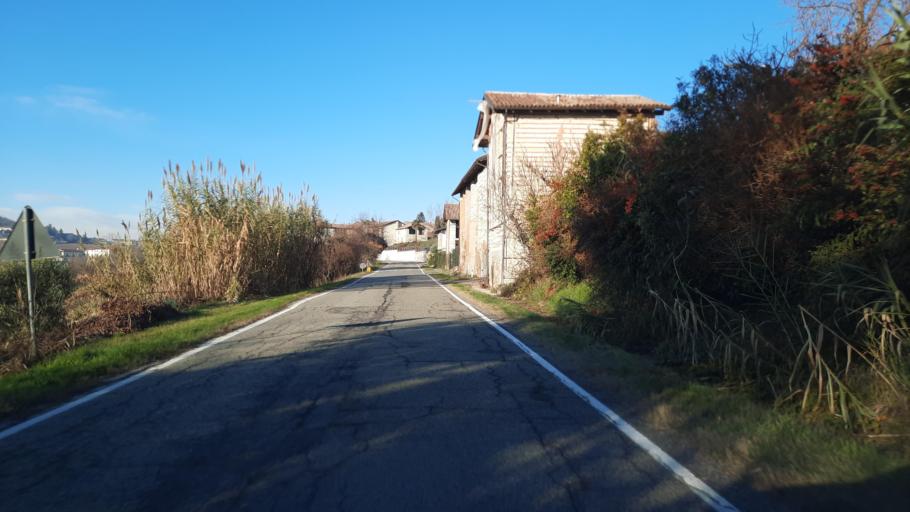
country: IT
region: Piedmont
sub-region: Provincia di Alessandria
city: Camino
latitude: 45.1553
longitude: 8.2931
